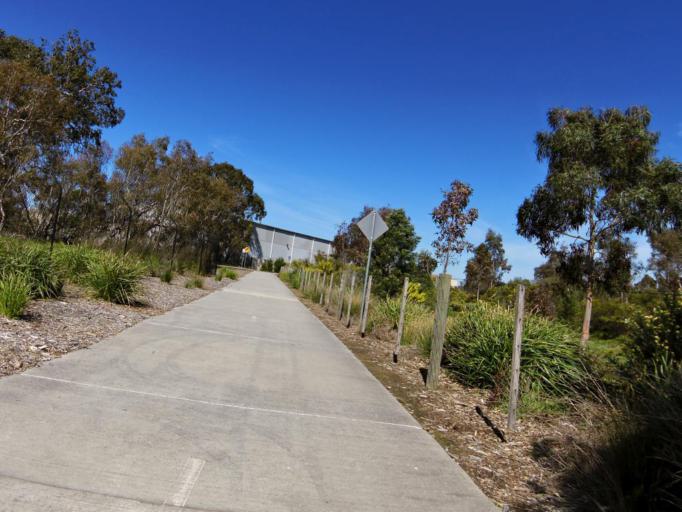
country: AU
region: Victoria
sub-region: Greater Dandenong
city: Dandenong
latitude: -37.9873
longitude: 145.1939
